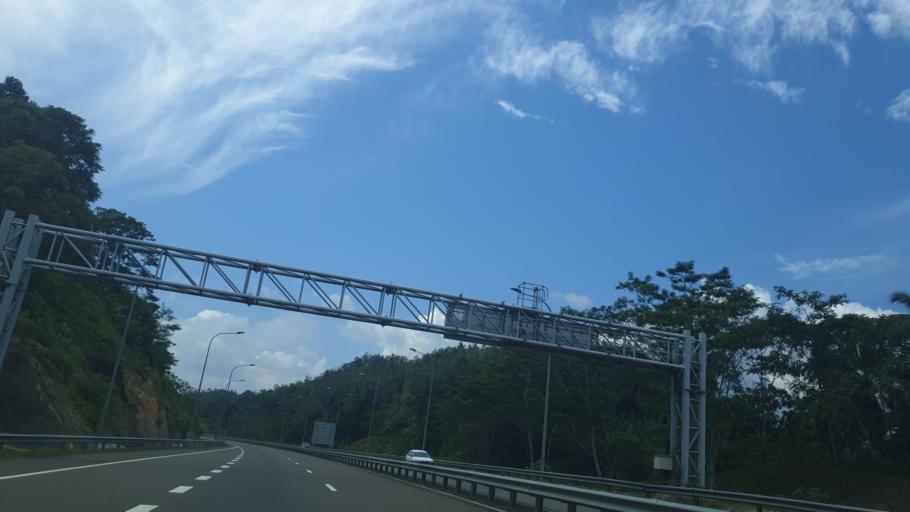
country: LK
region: Southern
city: Talpe
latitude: 6.0378
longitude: 80.3602
